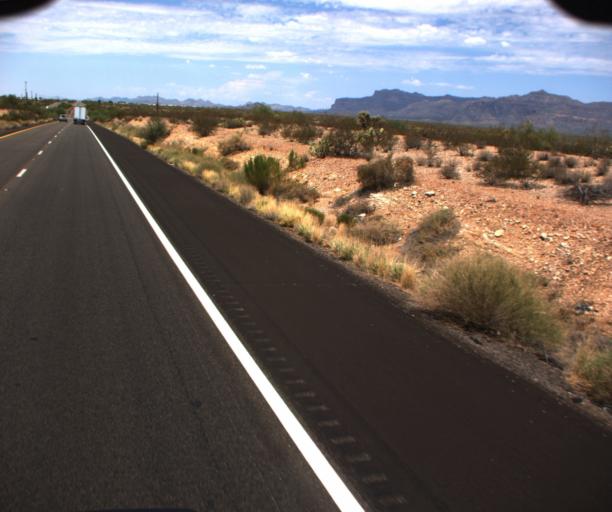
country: US
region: Arizona
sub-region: Pinal County
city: Gold Camp
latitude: 33.2884
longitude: -111.3800
